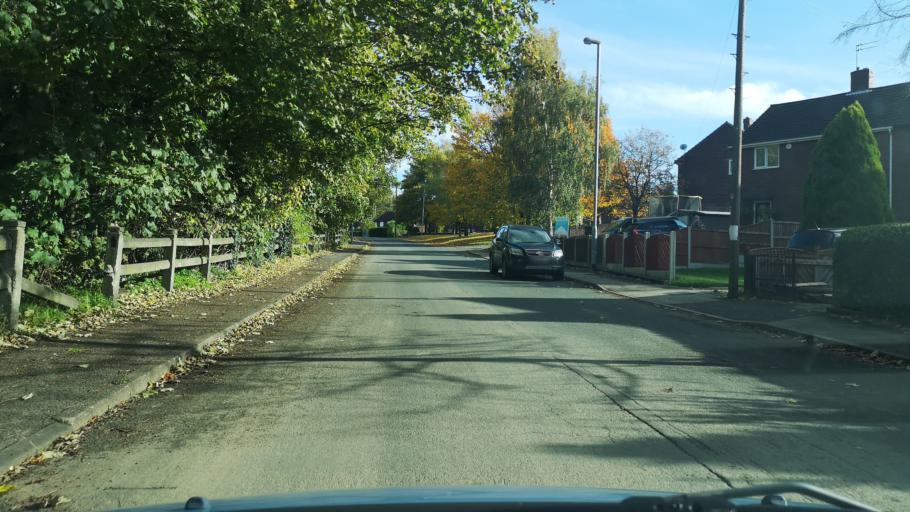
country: GB
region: England
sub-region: City and Borough of Wakefield
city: Low Ackworth
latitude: 53.6448
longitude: -1.3404
